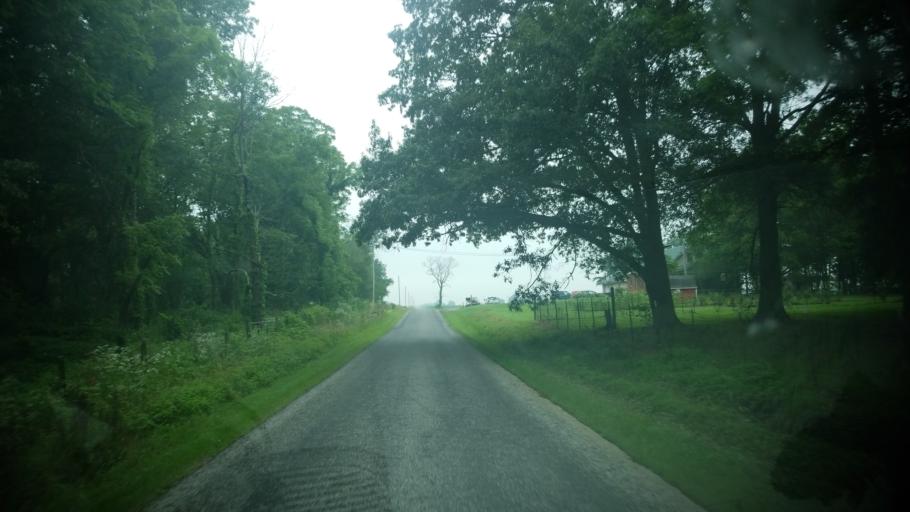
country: US
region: Illinois
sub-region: Clay County
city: Flora
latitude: 38.5735
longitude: -88.3911
